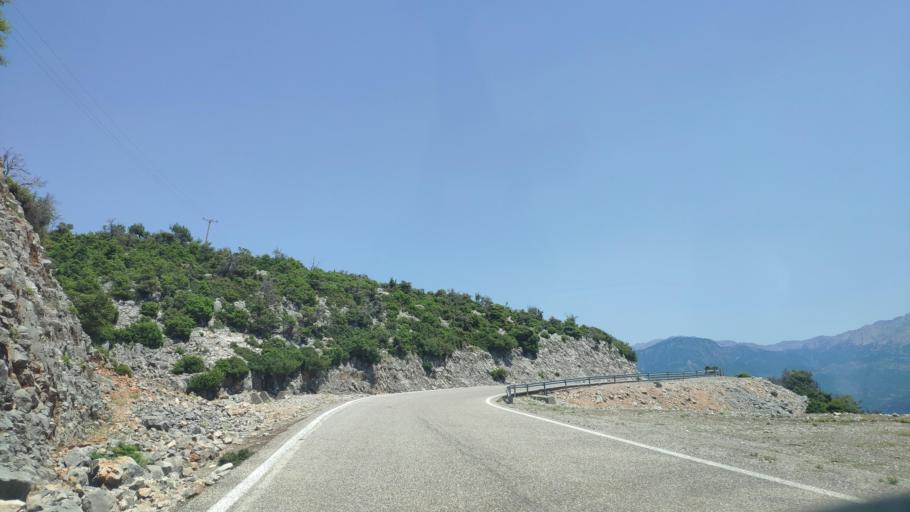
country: GR
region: West Greece
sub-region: Nomos Aitolias kai Akarnanias
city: Krikellos
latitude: 39.0551
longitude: 21.3835
